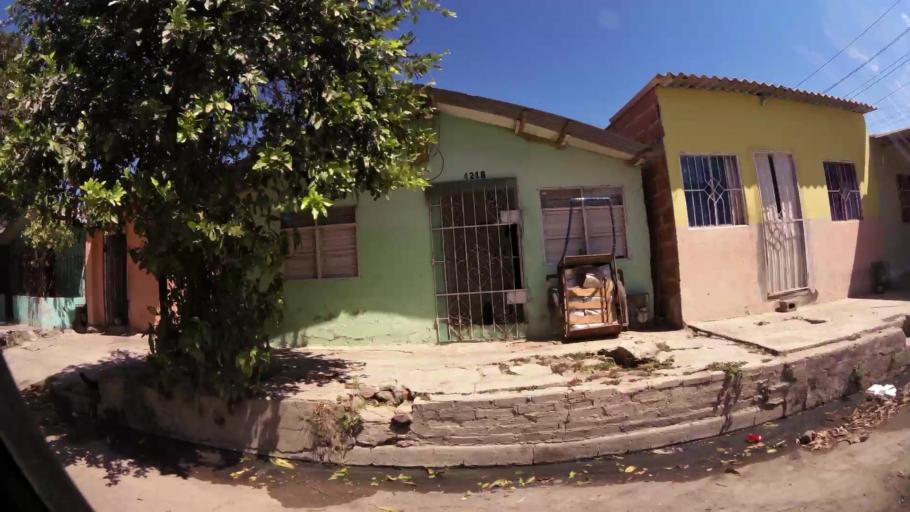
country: CO
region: Atlantico
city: Barranquilla
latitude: 10.9805
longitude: -74.7669
